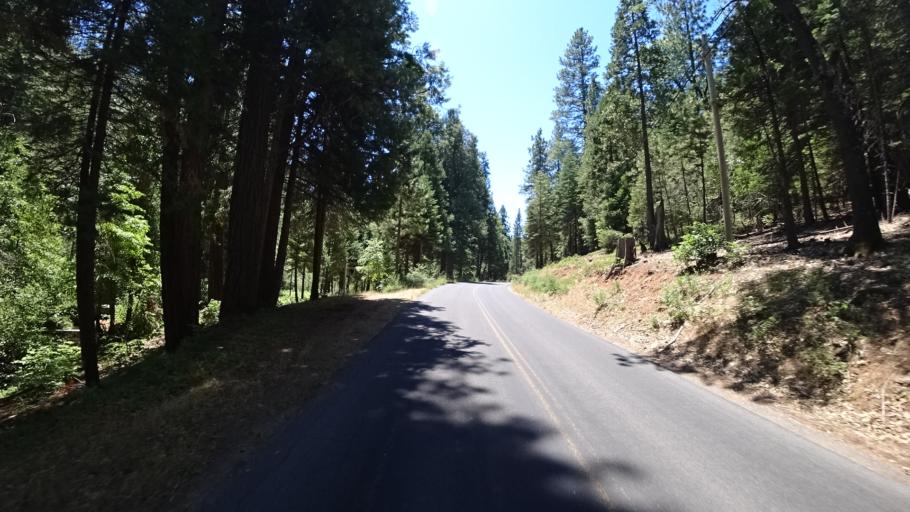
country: US
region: California
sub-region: Calaveras County
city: Arnold
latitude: 38.2415
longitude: -120.3421
